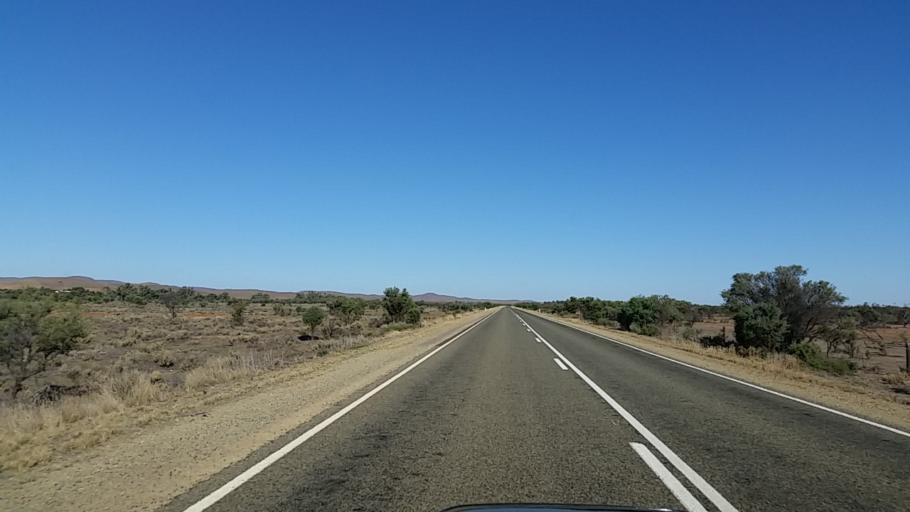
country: AU
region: South Australia
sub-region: Flinders Ranges
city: Quorn
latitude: -32.3877
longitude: 138.5043
